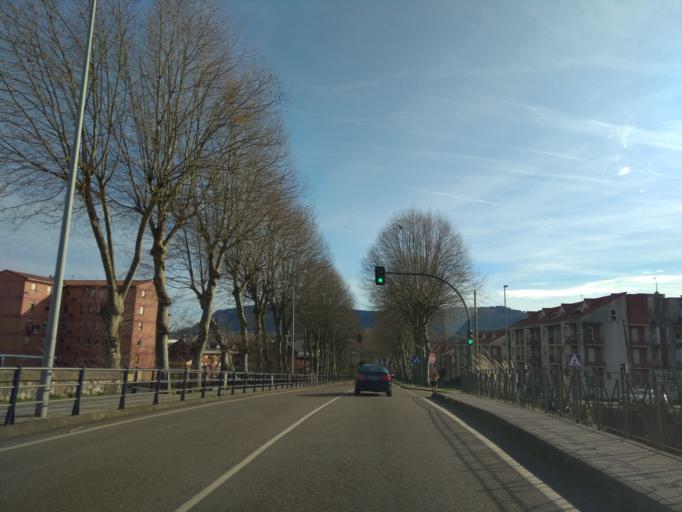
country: ES
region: Cantabria
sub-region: Provincia de Cantabria
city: El Astillero
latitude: 43.4071
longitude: -3.8418
